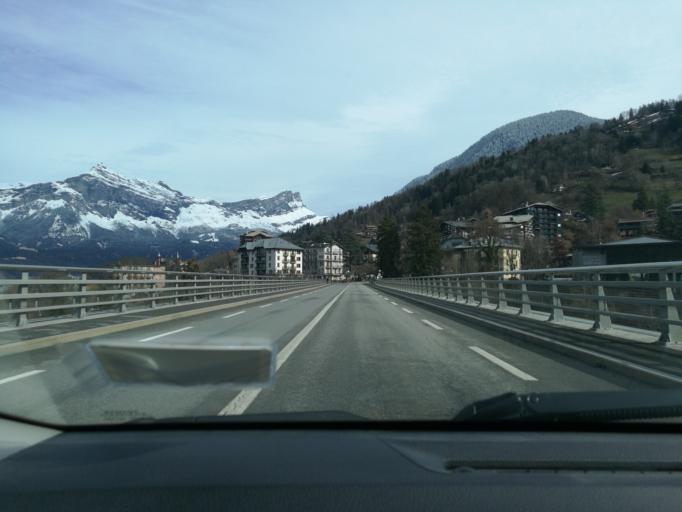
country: FR
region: Rhone-Alpes
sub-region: Departement de la Haute-Savoie
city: Saint-Gervais-les-Bains
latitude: 45.8931
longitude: 6.7090
